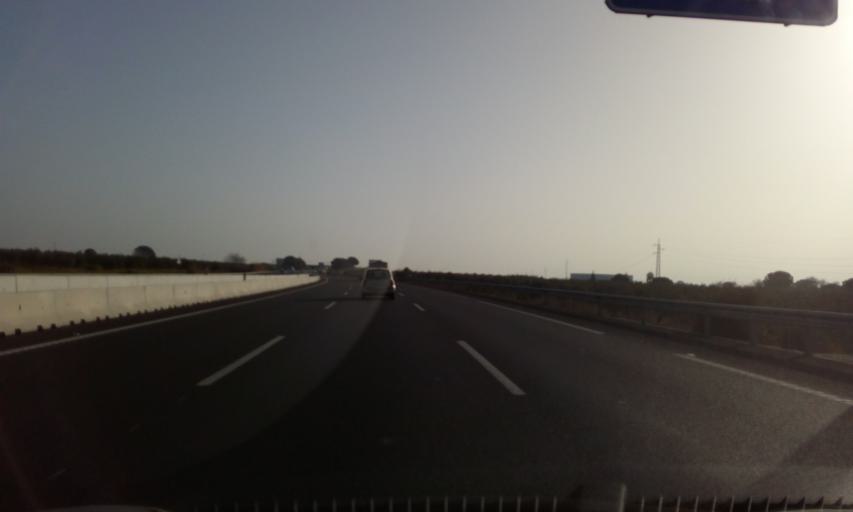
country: ES
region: Andalusia
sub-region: Provincia de Sevilla
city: Benacazon
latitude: 37.3579
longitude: -6.1892
